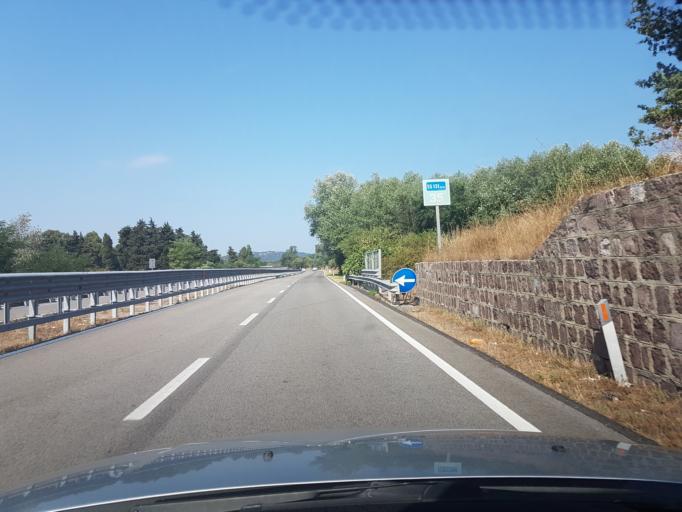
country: IT
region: Sardinia
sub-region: Provincia di Nuoro
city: Oniferi
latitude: 40.3116
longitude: 9.2107
